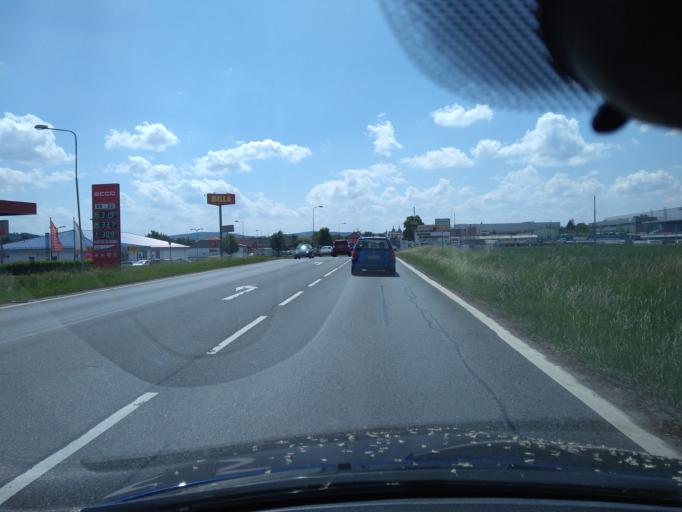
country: CZ
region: Plzensky
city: Prestice
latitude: 49.5835
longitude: 13.3268
